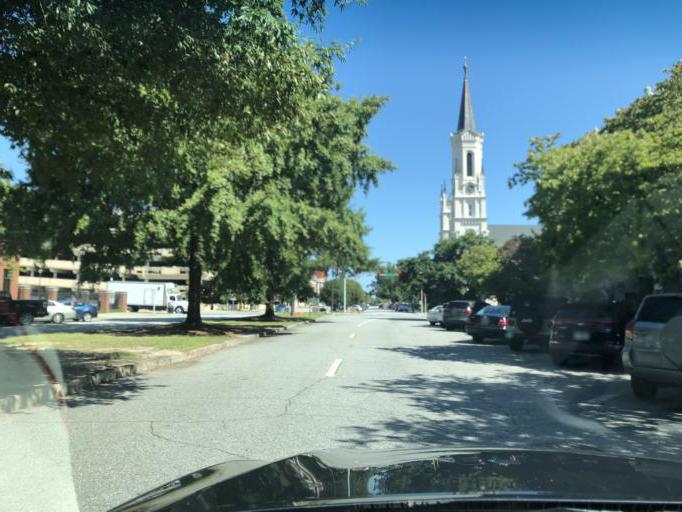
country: US
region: Georgia
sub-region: Muscogee County
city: Columbus
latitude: 32.4660
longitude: -84.9917
